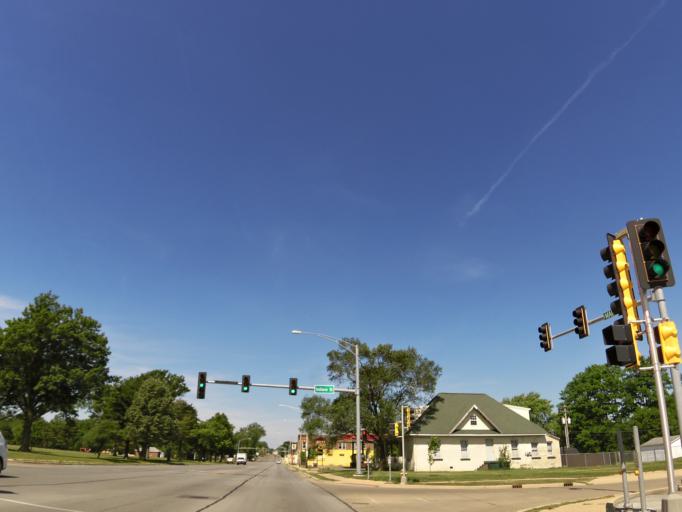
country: US
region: Illinois
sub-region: Vermilion County
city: Danville
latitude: 40.1320
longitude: -87.5882
